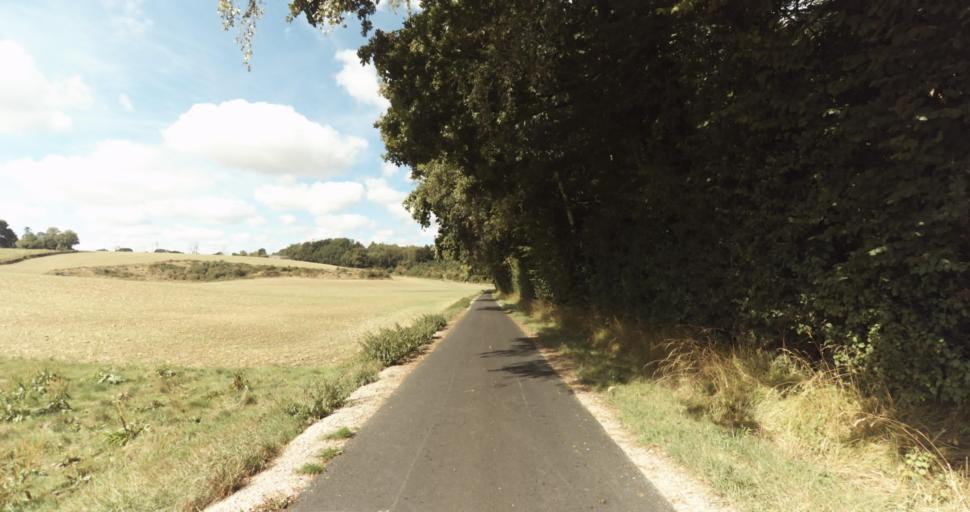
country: FR
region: Lower Normandy
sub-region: Departement du Calvados
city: Orbec
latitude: 48.9107
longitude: 0.3856
